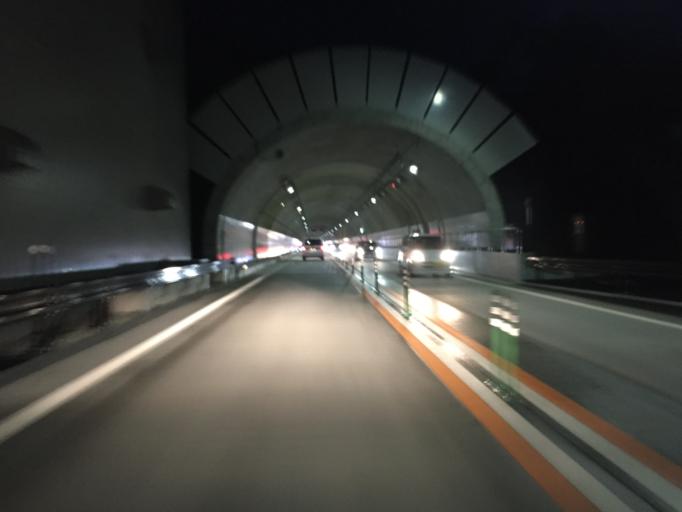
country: JP
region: Yamagata
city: Yonezawa
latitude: 37.8684
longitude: 140.2290
